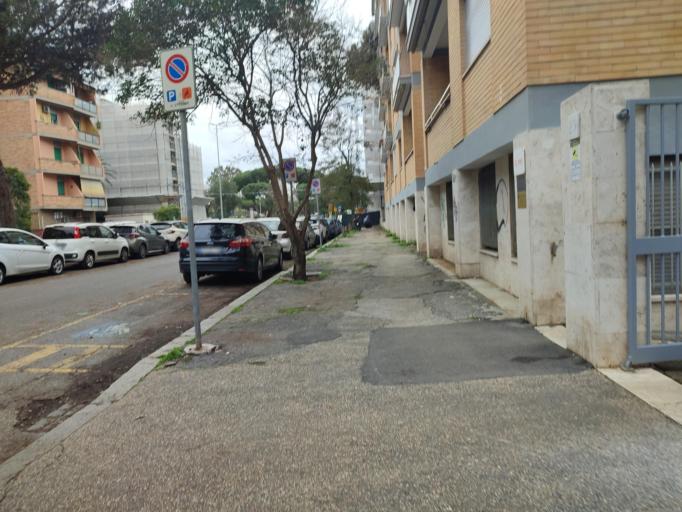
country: IT
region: Latium
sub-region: Citta metropolitana di Roma Capitale
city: Lido di Ostia
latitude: 41.7370
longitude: 12.2887
